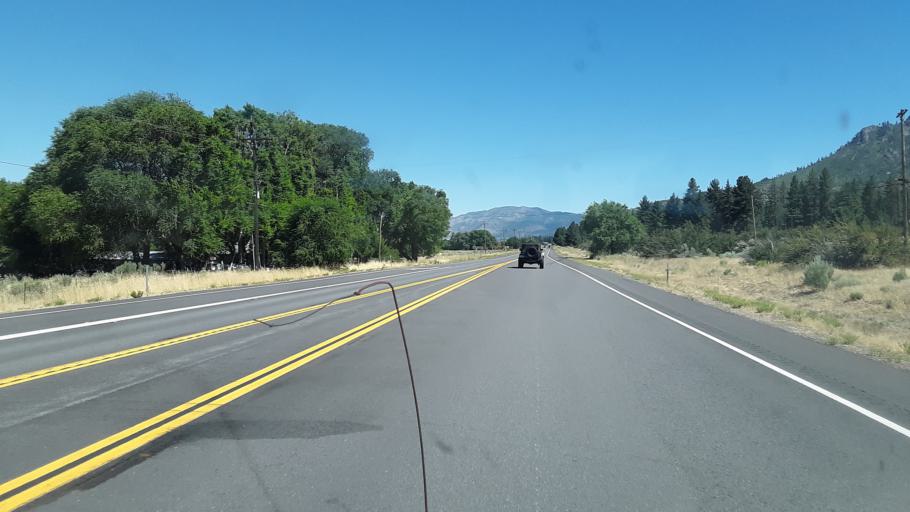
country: US
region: California
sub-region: Lassen County
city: Janesville
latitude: 40.2462
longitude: -120.4582
